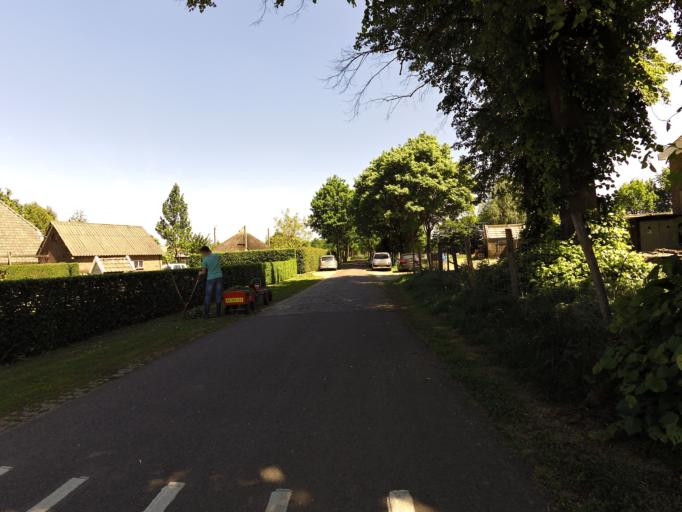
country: NL
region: Gelderland
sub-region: Gemeente Bronckhorst
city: Baak
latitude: 52.0633
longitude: 6.2325
